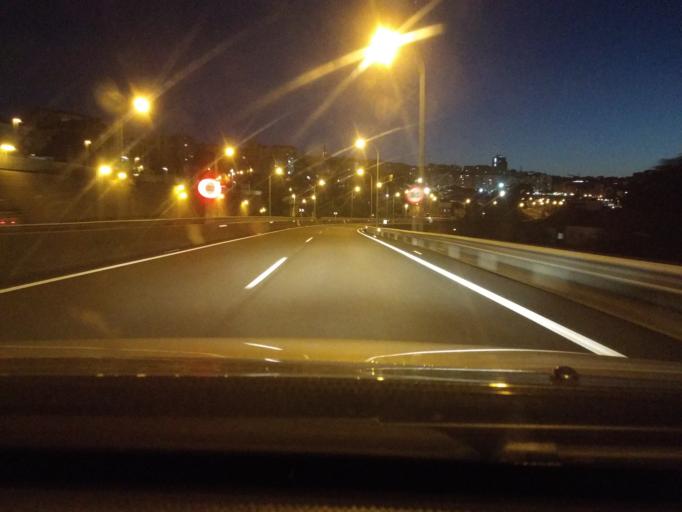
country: ES
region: Galicia
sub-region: Provincia de Pontevedra
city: Vigo
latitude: 42.2405
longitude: -8.7050
